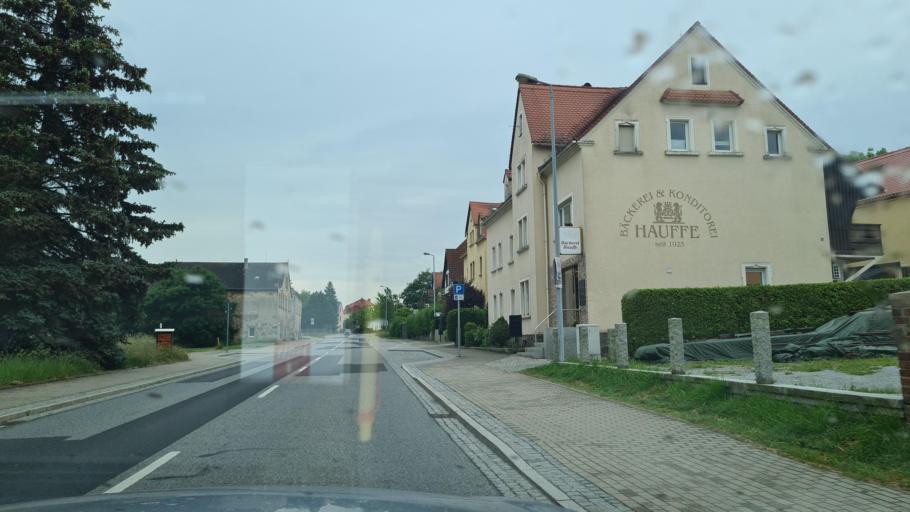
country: DE
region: Saxony
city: Grosspostwitz
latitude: 51.1155
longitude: 14.4426
